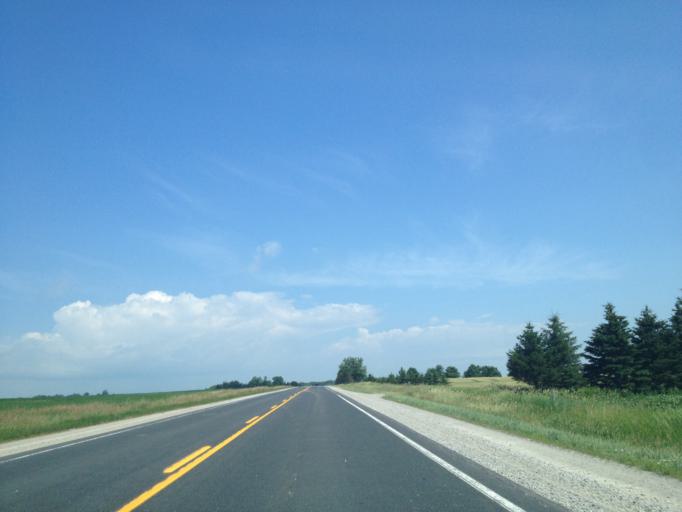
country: CA
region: Ontario
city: Huron East
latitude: 43.4270
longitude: -81.2239
